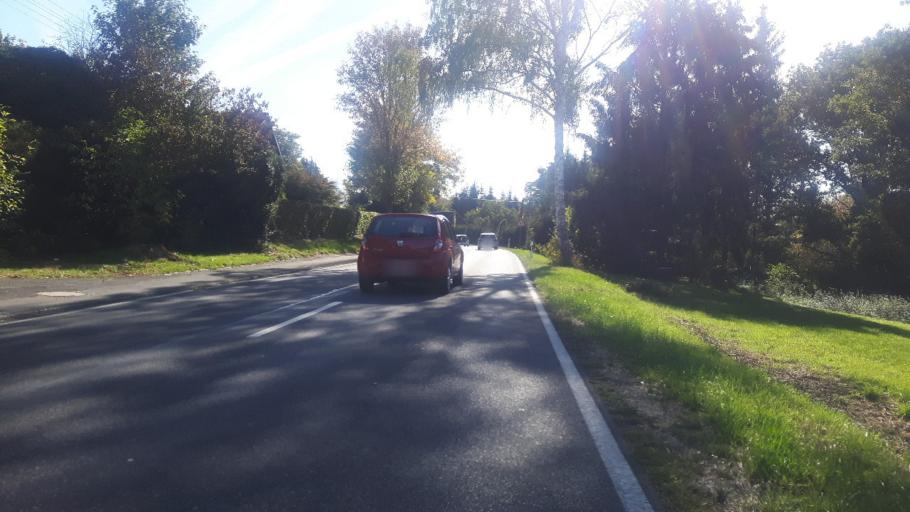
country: DE
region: Rheinland-Pfalz
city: Furthen
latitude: 50.7848
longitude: 7.6248
